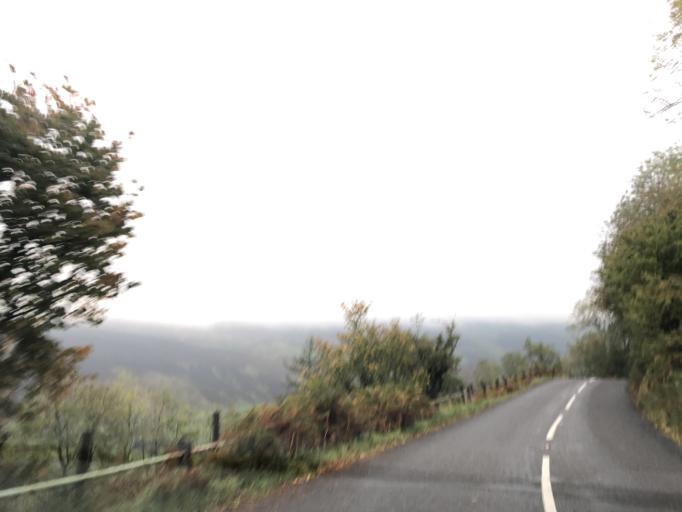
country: GB
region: England
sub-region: Cumbria
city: Ambleside
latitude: 54.4459
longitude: -2.9034
